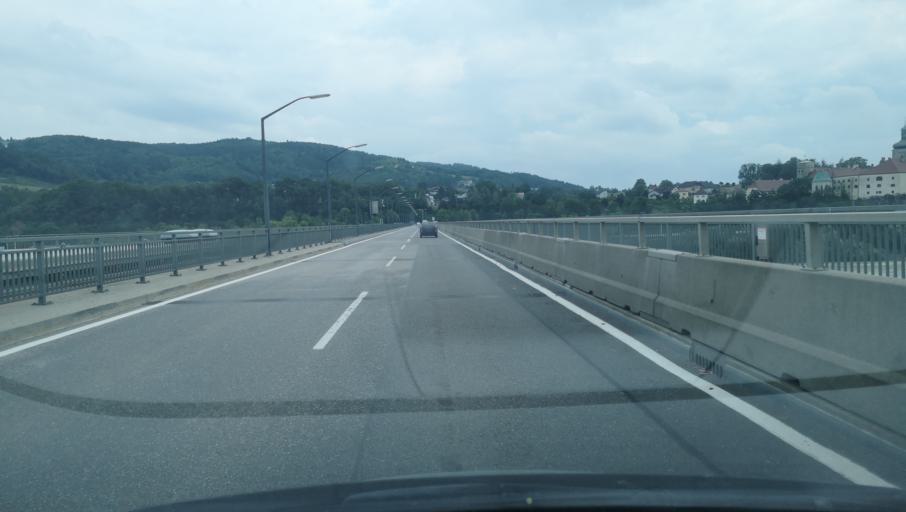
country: AT
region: Lower Austria
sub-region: Politischer Bezirk Melk
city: Ybbs an der Donau
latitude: 48.1892
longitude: 15.0685
